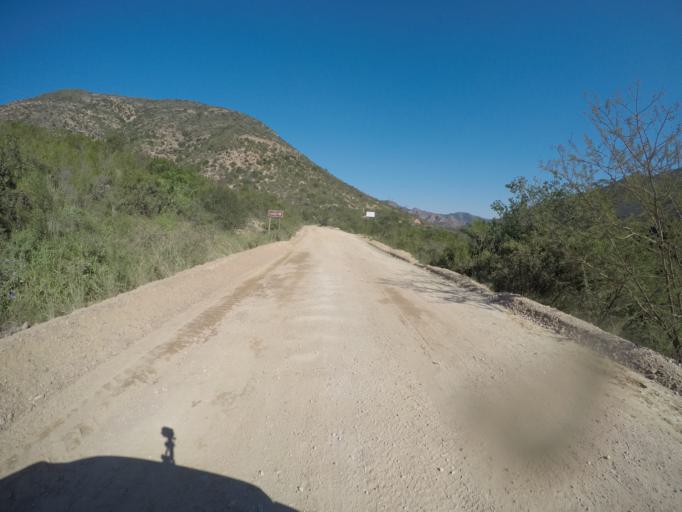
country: ZA
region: Eastern Cape
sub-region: Cacadu District Municipality
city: Kruisfontein
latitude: -33.6636
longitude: 24.5561
